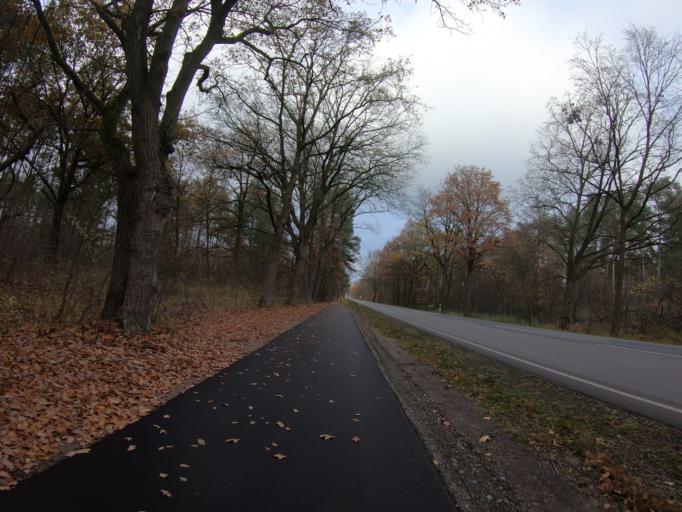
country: DE
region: Lower Saxony
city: Wesendorf
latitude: 52.5765
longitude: 10.5267
